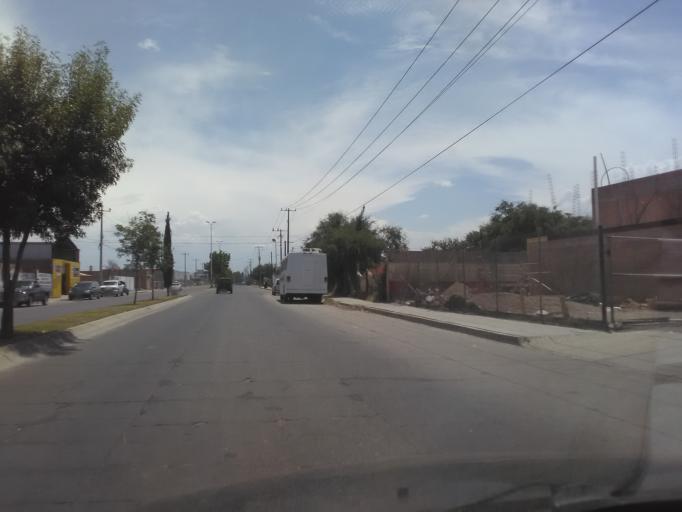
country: MX
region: Durango
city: Victoria de Durango
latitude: 24.0240
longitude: -104.6208
